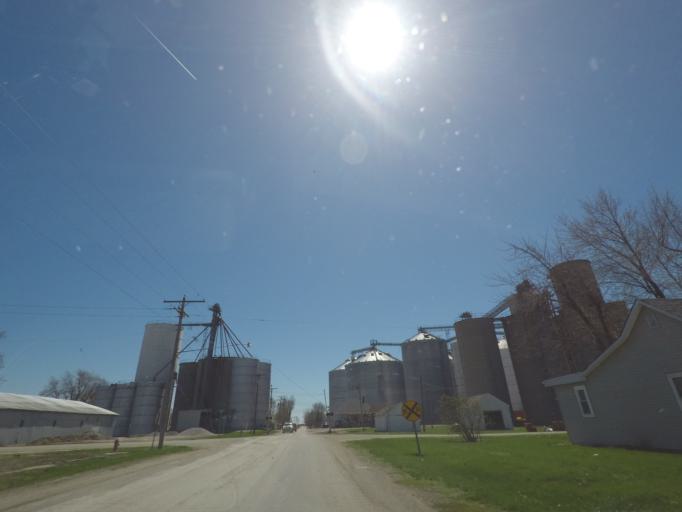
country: US
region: Illinois
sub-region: Macon County
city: Warrensburg
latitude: 39.9667
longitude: -89.1627
